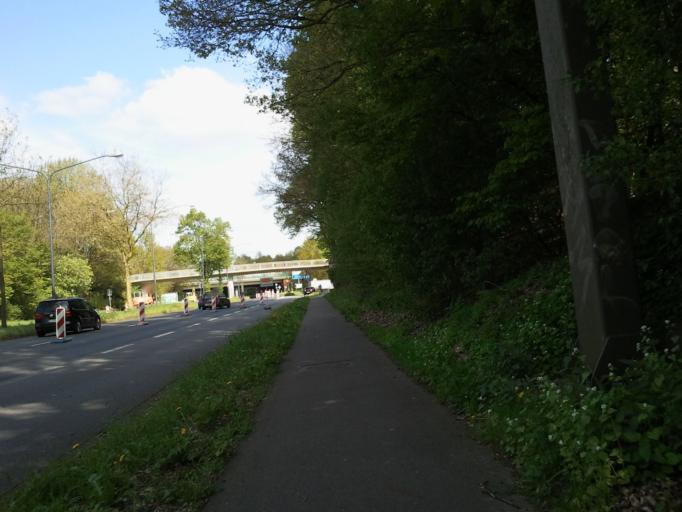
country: DE
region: Lower Saxony
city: Lilienthal
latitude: 53.0820
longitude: 8.9035
